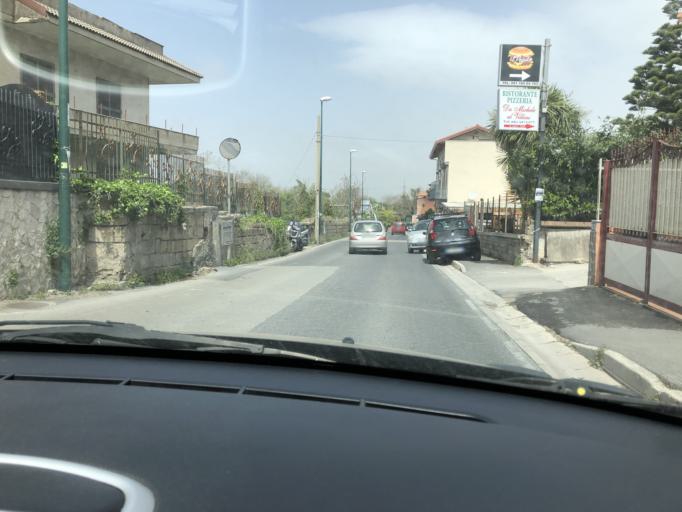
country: IT
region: Campania
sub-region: Provincia di Napoli
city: Torre Caracciolo
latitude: 40.8743
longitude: 14.1868
